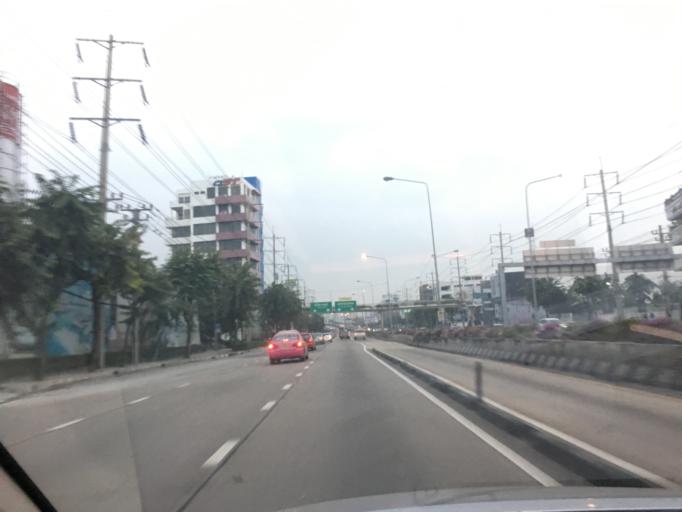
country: TH
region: Bangkok
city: Rat Burana
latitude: 13.6883
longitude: 100.5151
